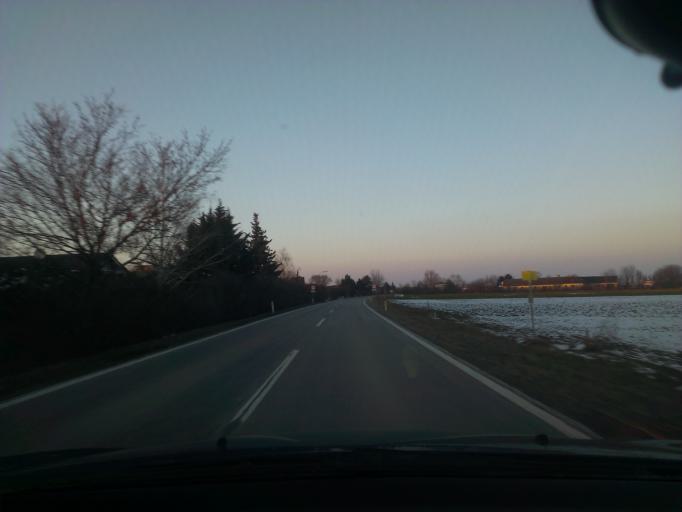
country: AT
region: Lower Austria
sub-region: Politischer Bezirk Baden
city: Reisenberg
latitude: 47.9901
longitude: 16.5191
